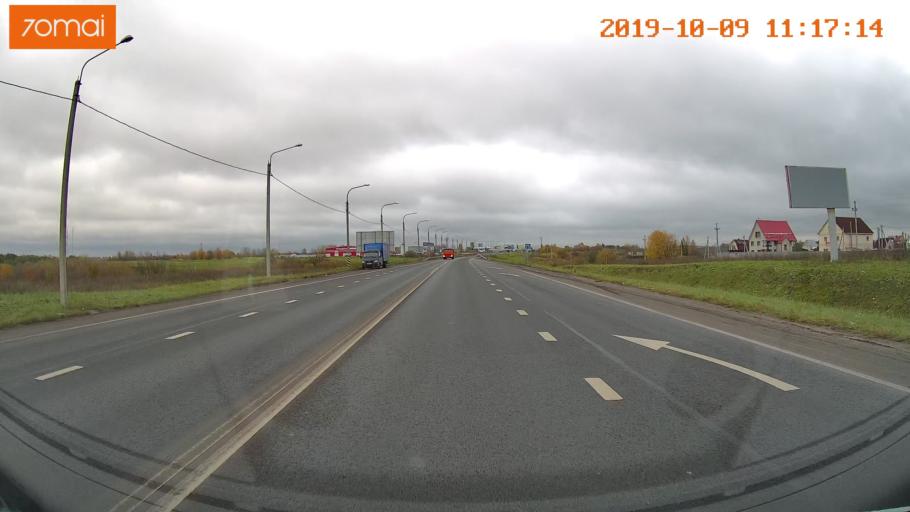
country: RU
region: Vologda
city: Vologda
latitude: 59.1752
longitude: 39.8957
